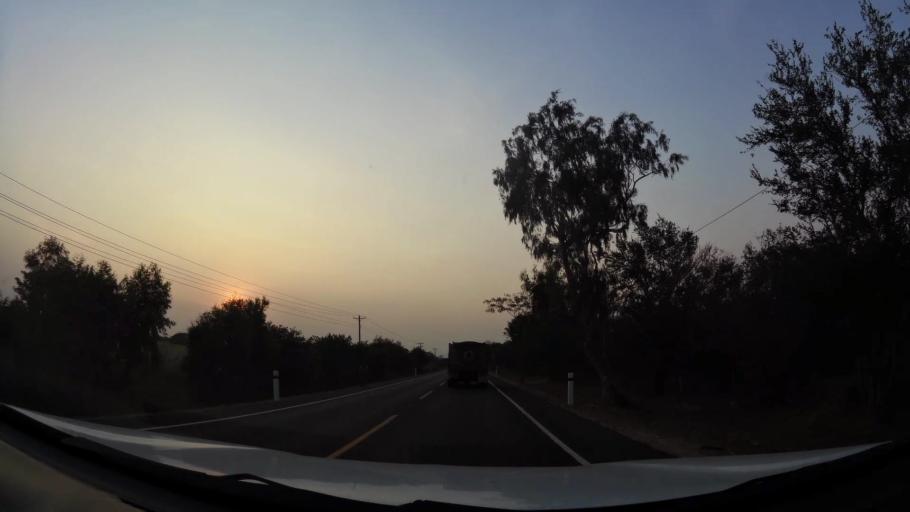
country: NI
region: Leon
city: La Paz Centro
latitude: 12.3143
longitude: -86.7876
